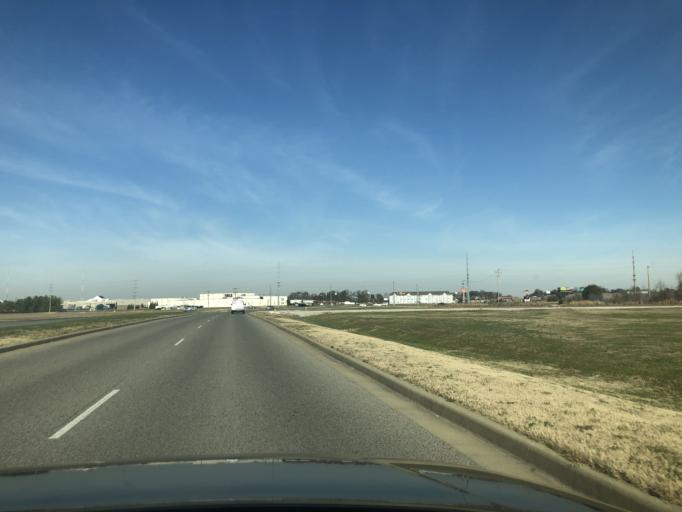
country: US
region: Indiana
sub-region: Vanderburgh County
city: Melody Hill
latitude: 37.9886
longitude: -87.4661
